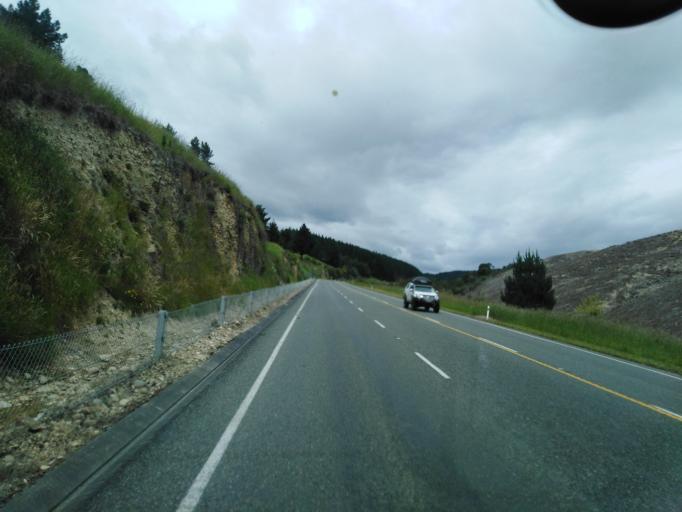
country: NZ
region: Tasman
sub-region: Tasman District
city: Wakefield
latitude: -41.4695
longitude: 172.9428
